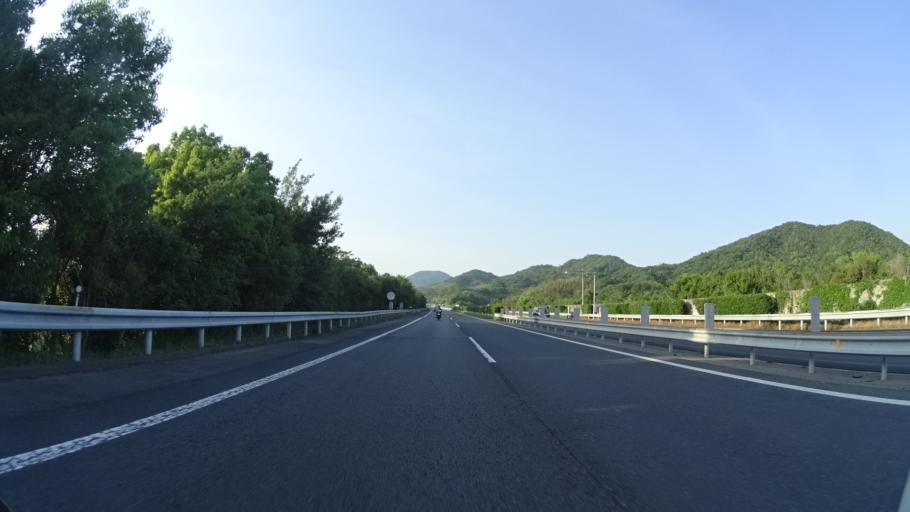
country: JP
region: Kagawa
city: Kan'onjicho
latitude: 34.1736
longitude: 133.7336
